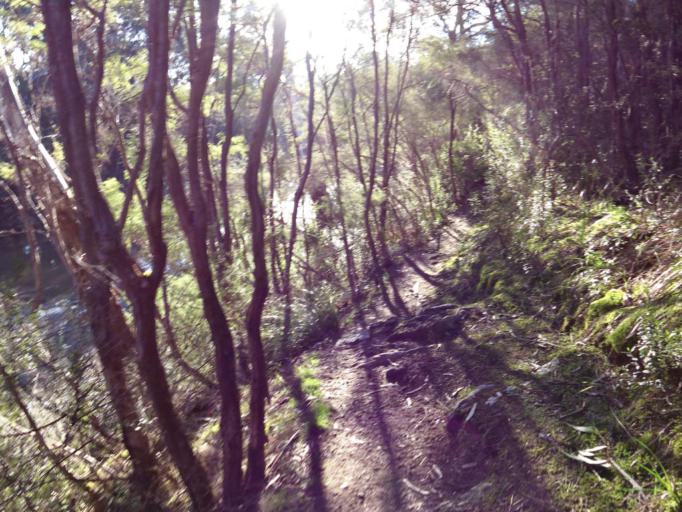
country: AU
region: Victoria
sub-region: Manningham
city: Warrandyte
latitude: -37.7334
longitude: 145.2431
